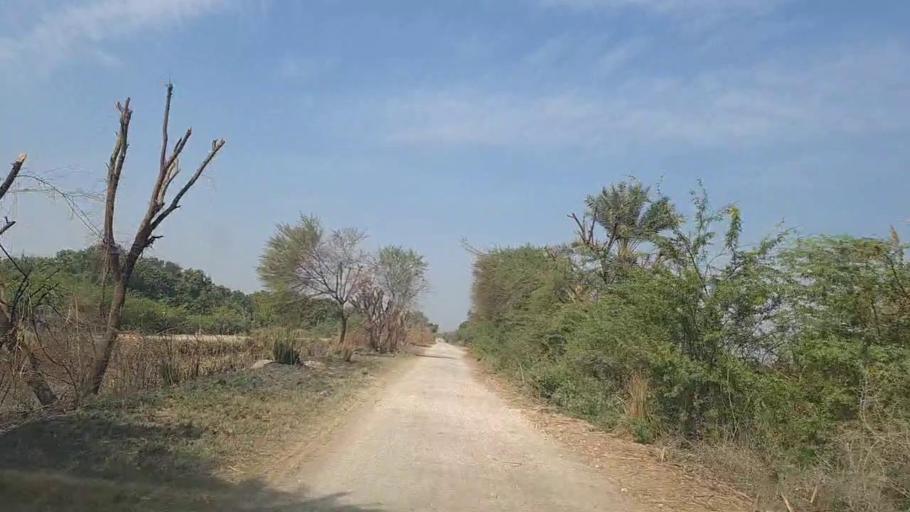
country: PK
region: Sindh
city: Mirpur Khas
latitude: 25.4899
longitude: 68.9212
